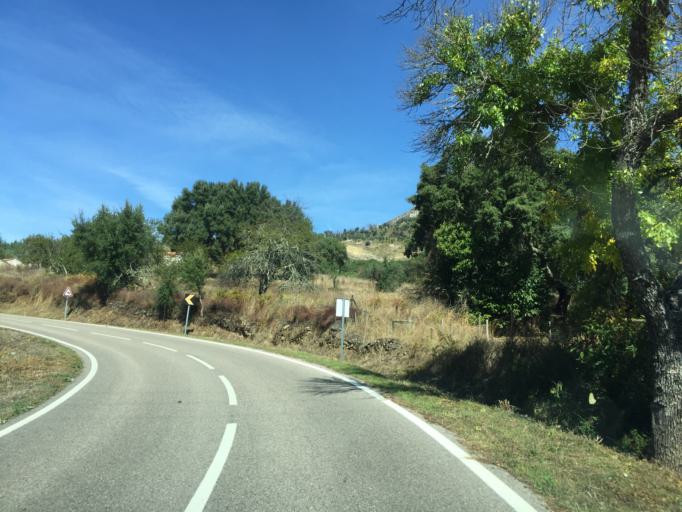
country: PT
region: Portalegre
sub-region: Marvao
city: Marvao
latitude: 39.3868
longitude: -7.3849
